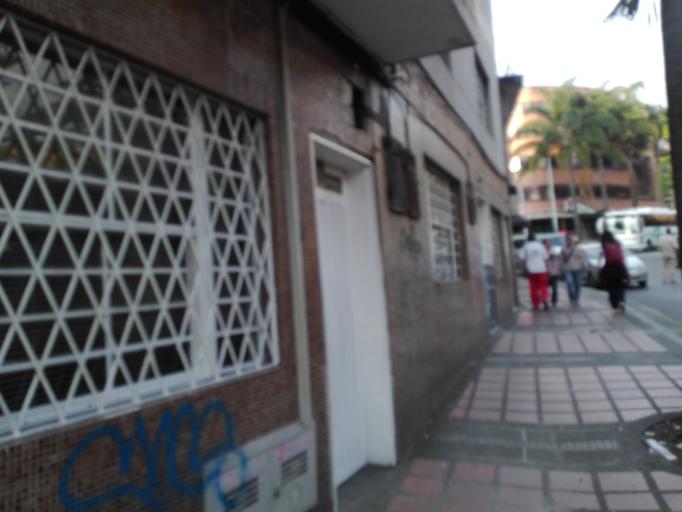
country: CO
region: Antioquia
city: Medellin
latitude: 6.2476
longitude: -75.5603
